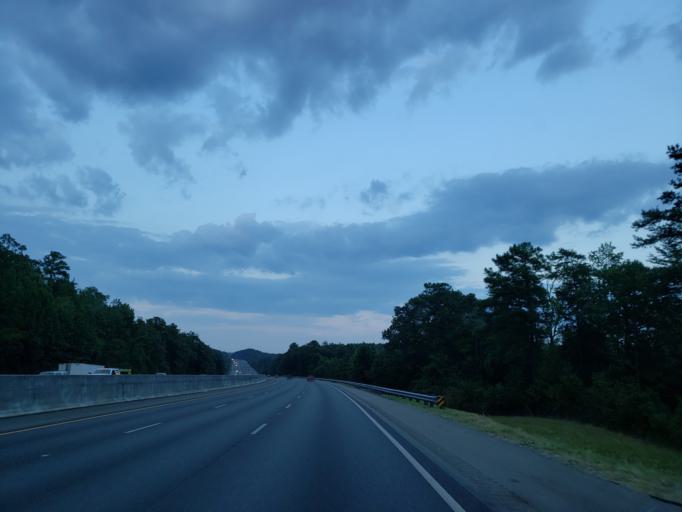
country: US
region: Alabama
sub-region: Bibb County
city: North Bibb
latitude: 33.2136
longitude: -87.1971
